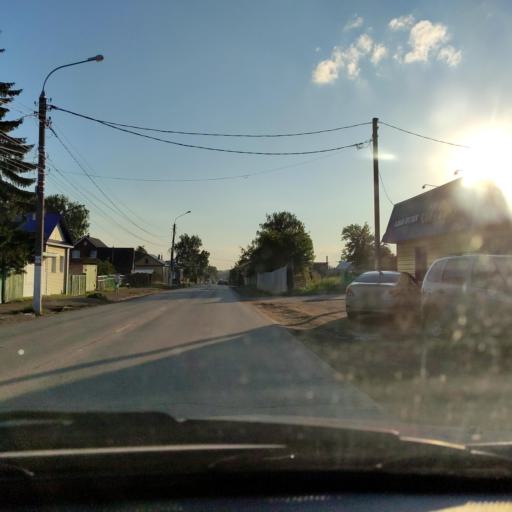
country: RU
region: Bashkortostan
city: Blagoveshchensk
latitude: 55.0322
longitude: 55.9820
